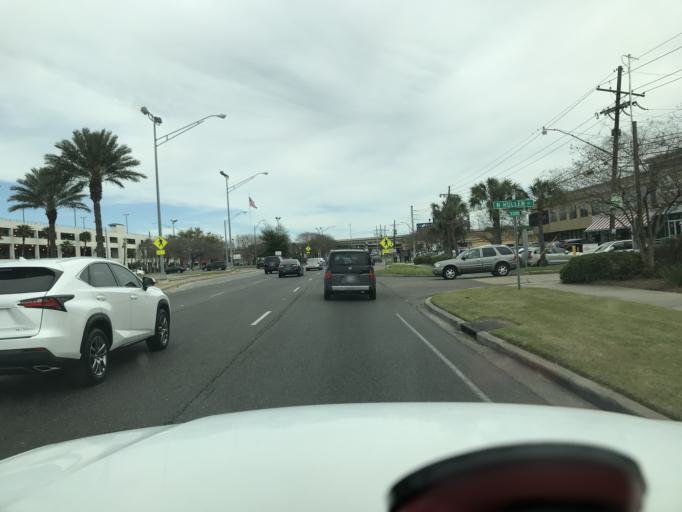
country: US
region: Louisiana
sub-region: Jefferson Parish
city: Metairie
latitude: 30.0032
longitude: -90.1586
